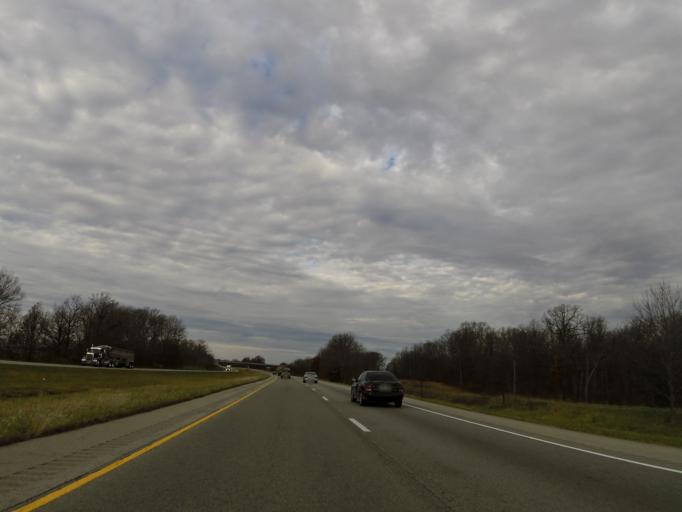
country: US
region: Illinois
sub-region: Clinton County
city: Wamac
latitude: 38.3840
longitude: -89.1217
